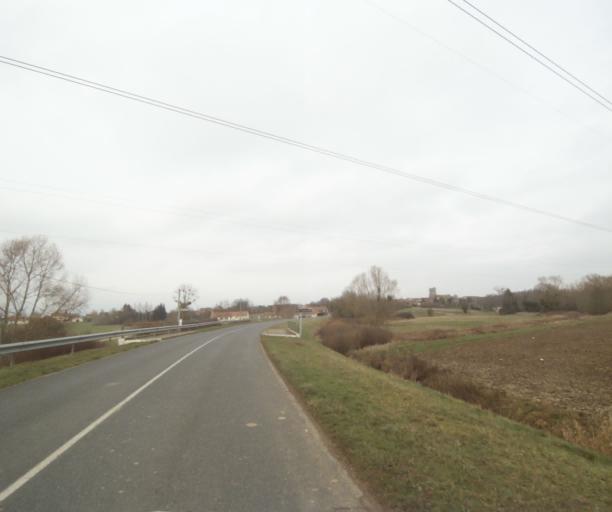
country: FR
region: Champagne-Ardenne
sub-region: Departement de la Marne
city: Pargny-sur-Saulx
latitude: 48.7439
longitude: 4.8487
